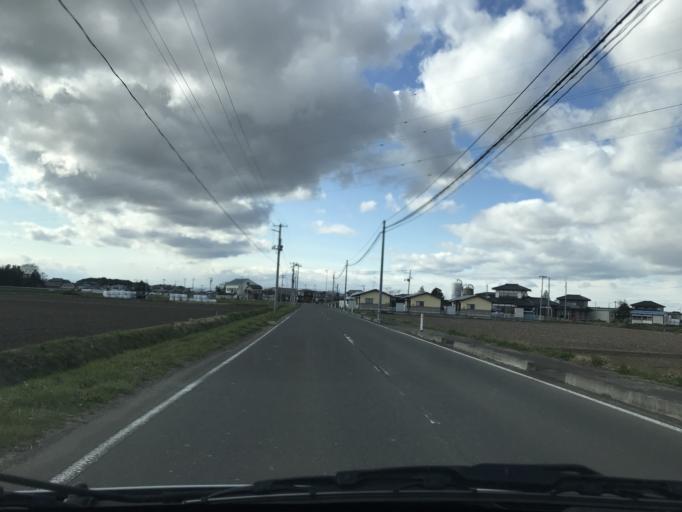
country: JP
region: Miyagi
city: Wakuya
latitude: 38.6635
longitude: 141.1831
